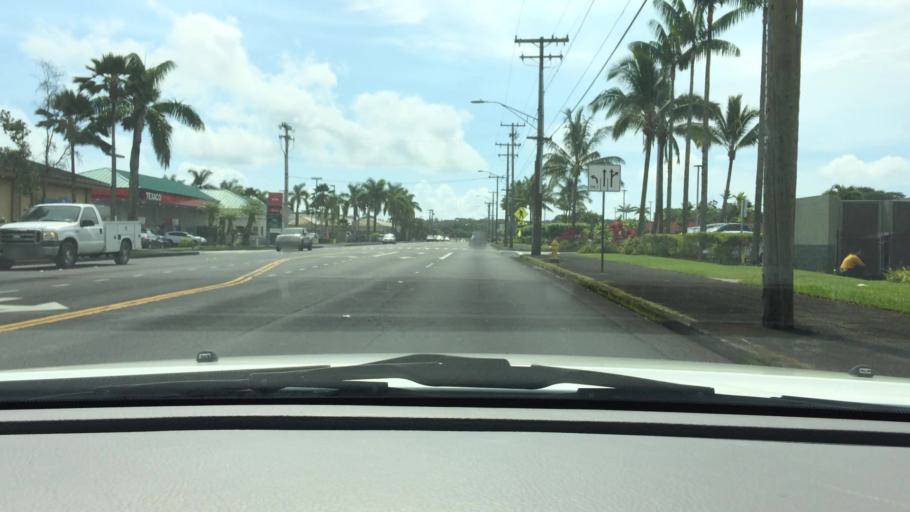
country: US
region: Hawaii
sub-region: Hawaii County
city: Hilo
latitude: 19.6992
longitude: -155.0644
